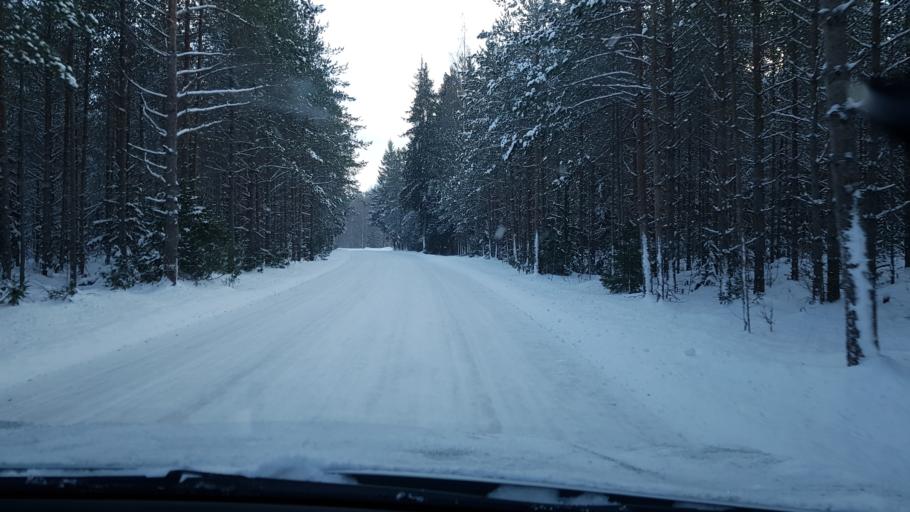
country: EE
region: Harju
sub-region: Nissi vald
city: Turba
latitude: 59.1752
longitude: 24.1329
